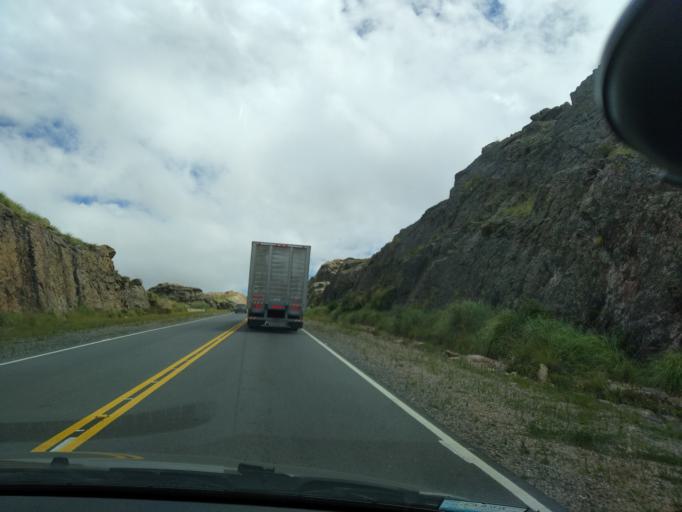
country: AR
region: Cordoba
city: Mina Clavero
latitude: -31.6454
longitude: -64.9029
